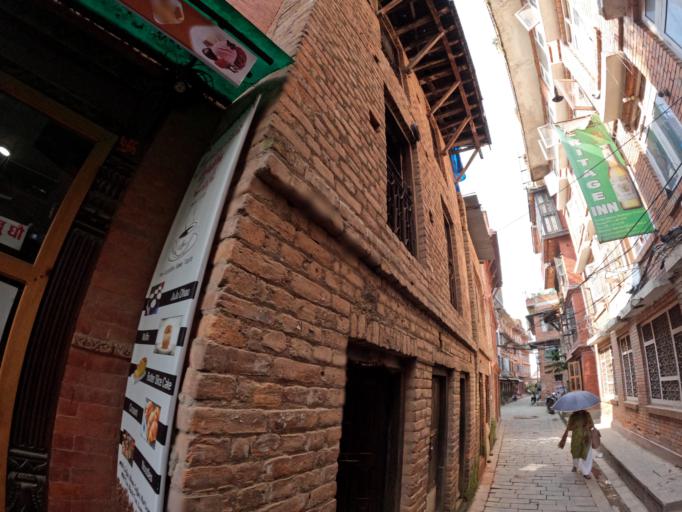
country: NP
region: Central Region
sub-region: Bagmati Zone
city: Bhaktapur
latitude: 27.6729
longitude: 85.4292
